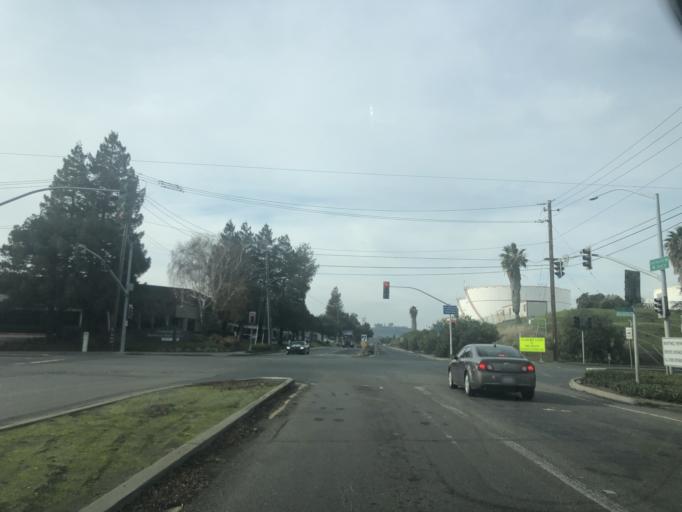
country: US
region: California
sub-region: Contra Costa County
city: Pacheco
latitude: 38.0025
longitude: -122.0533
